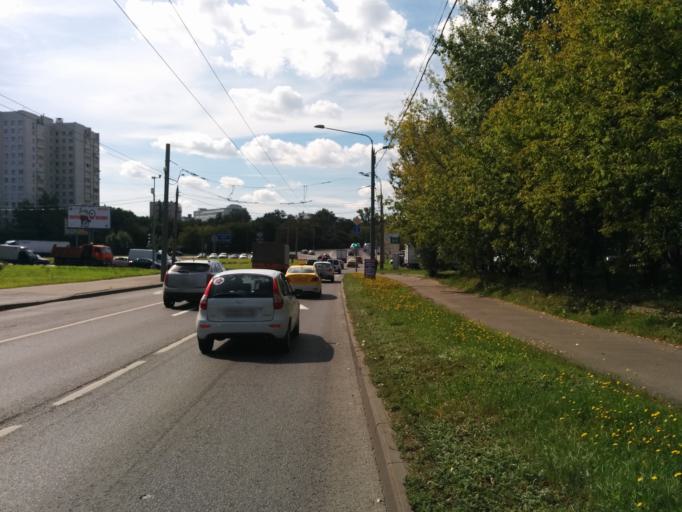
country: RU
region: Moscow
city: Mar'ina Roshcha
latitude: 55.8135
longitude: 37.6183
